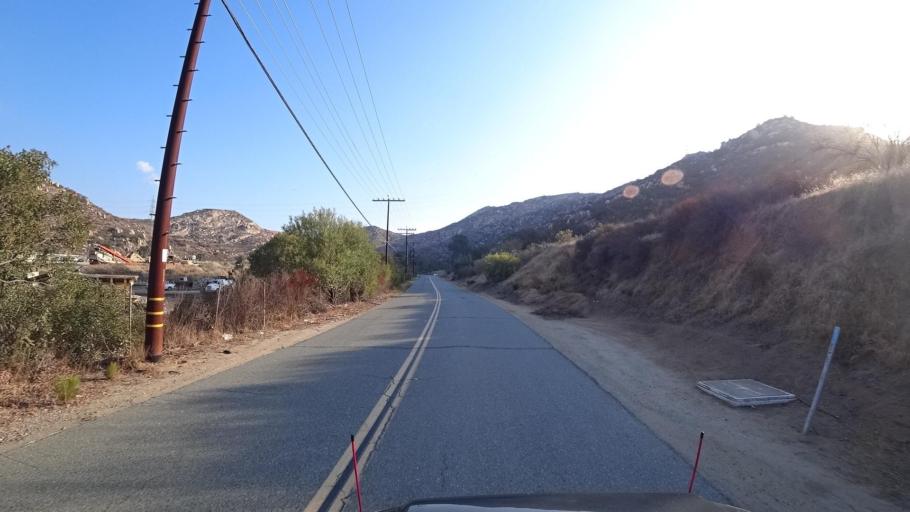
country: US
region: California
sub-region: San Diego County
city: Eucalyptus Hills
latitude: 32.9022
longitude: -116.9303
